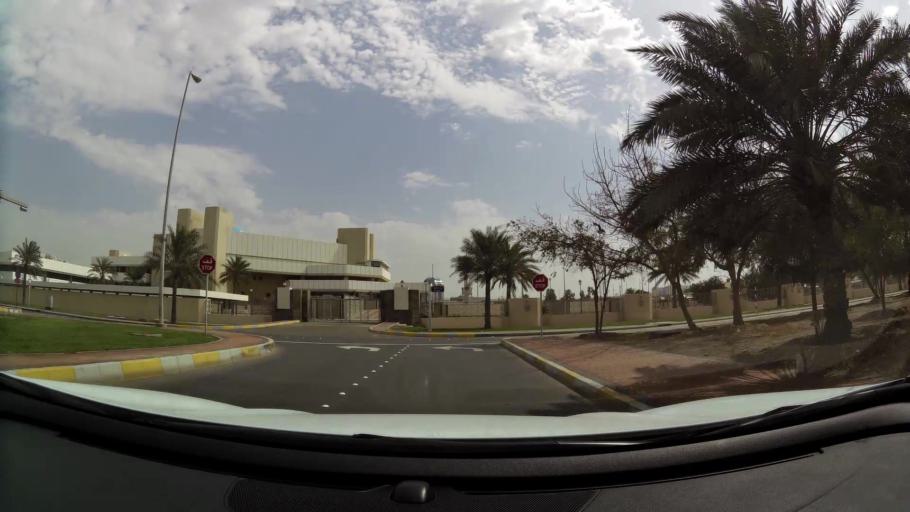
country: AE
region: Abu Dhabi
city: Abu Dhabi
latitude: 24.4640
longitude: 54.3306
